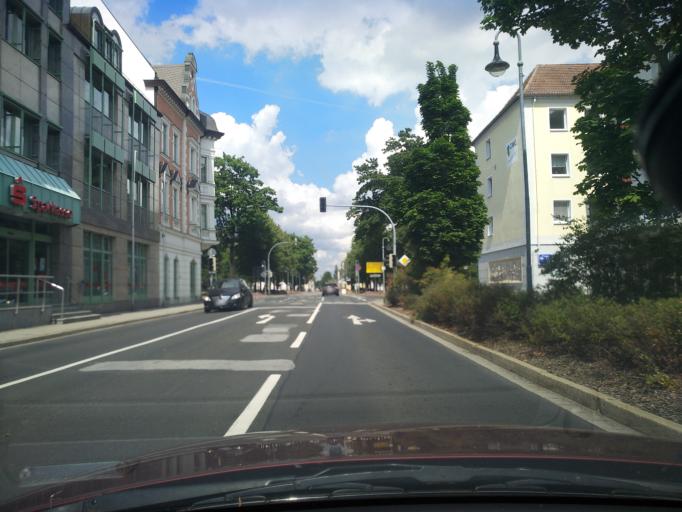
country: DE
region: Saxony
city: Niesky
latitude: 51.2918
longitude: 14.8221
